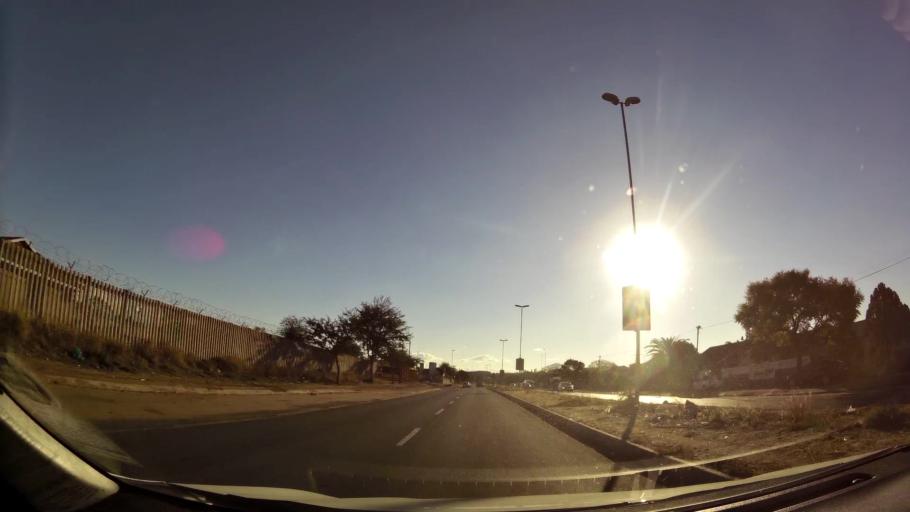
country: ZA
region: Limpopo
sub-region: Capricorn District Municipality
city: Polokwane
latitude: -23.8534
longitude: 29.3948
